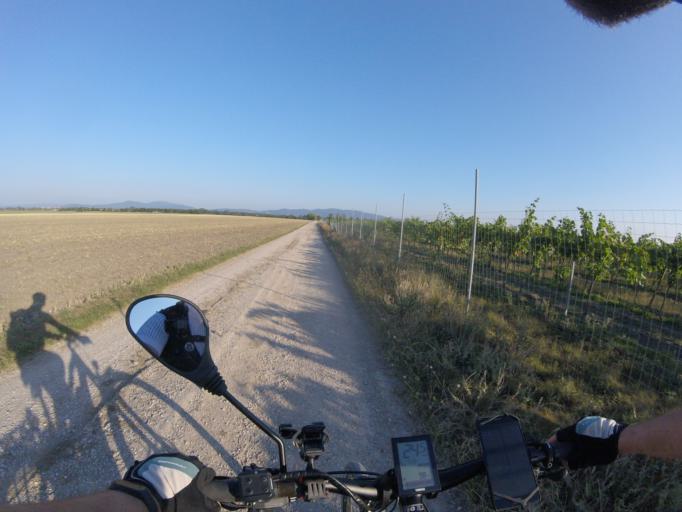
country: AT
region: Lower Austria
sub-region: Politischer Bezirk Baden
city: Trumau
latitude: 47.9836
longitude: 16.3532
